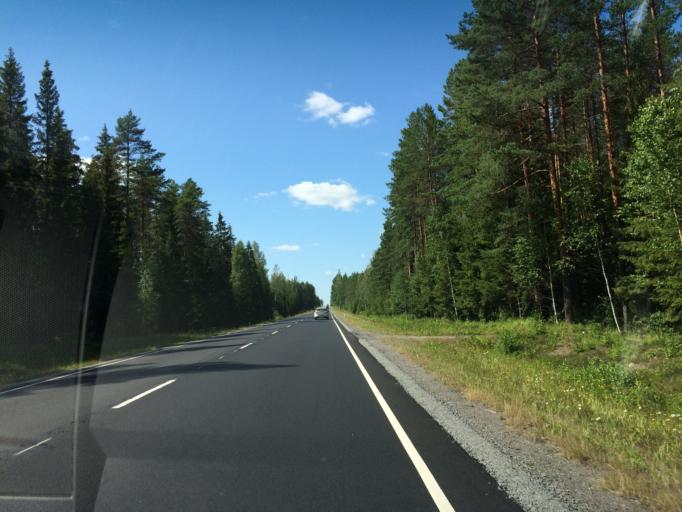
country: FI
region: Pirkanmaa
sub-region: Lounais-Pirkanmaa
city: Kiikoinen
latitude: 61.4738
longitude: 22.4964
